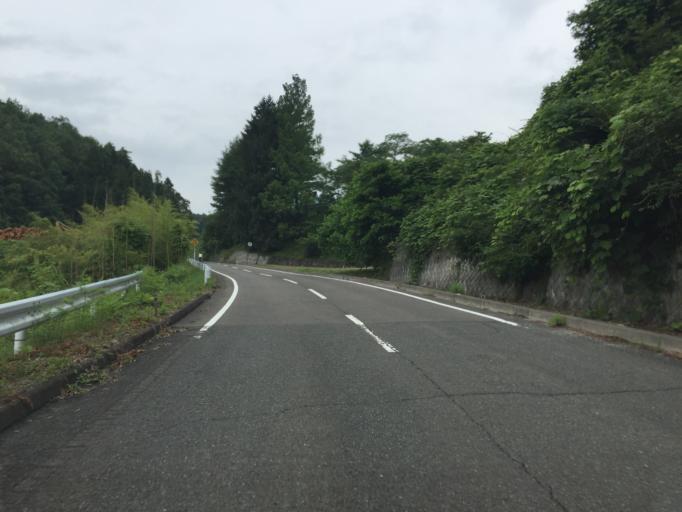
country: JP
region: Fukushima
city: Fukushima-shi
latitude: 37.6515
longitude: 140.5811
